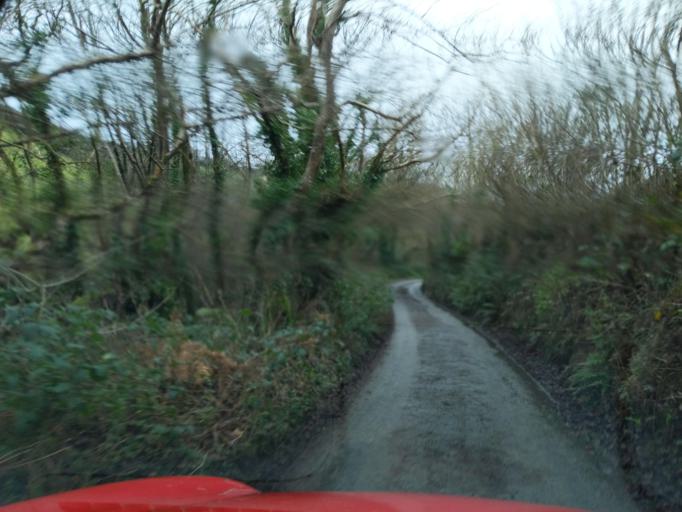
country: GB
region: England
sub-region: Cornwall
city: Duloe
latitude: 50.3484
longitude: -4.5175
